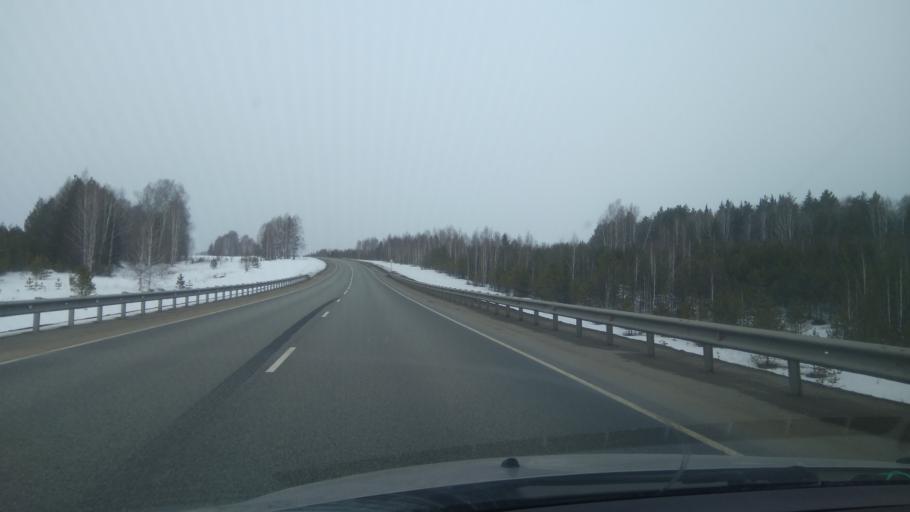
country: RU
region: Perm
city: Suksun
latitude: 56.9267
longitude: 57.5583
